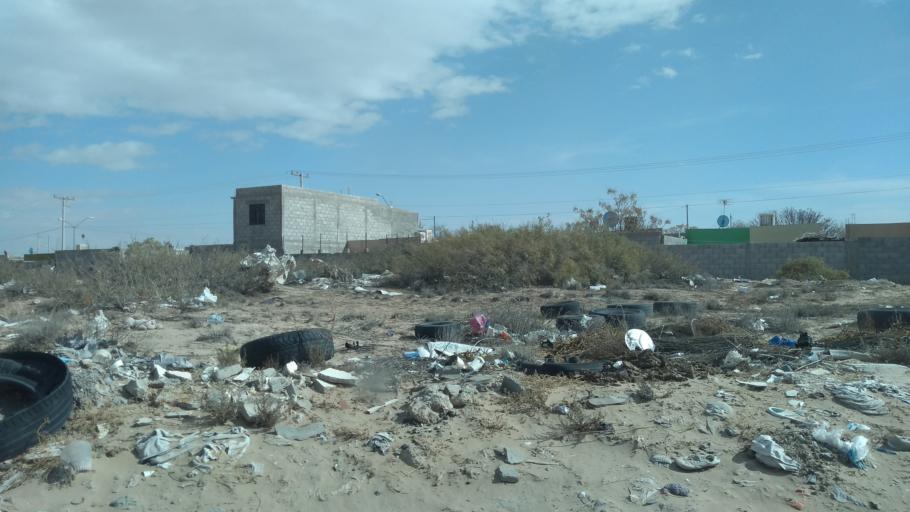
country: US
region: Texas
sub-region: El Paso County
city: San Elizario
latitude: 31.5690
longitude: -106.3421
